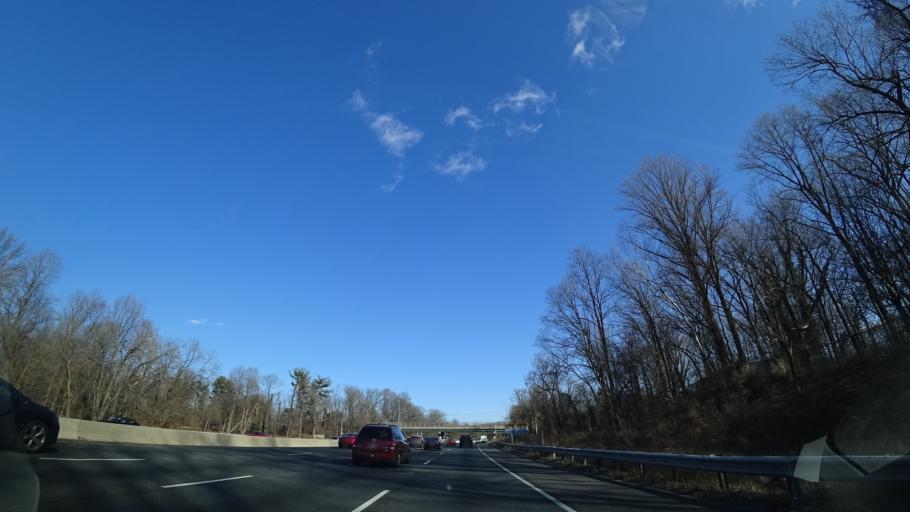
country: US
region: Maryland
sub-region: Montgomery County
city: Cabin John
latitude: 38.9809
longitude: -77.1751
